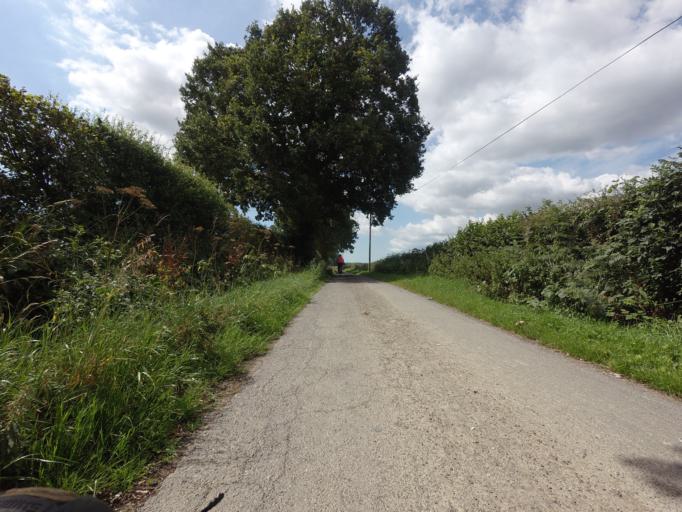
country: GB
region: England
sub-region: Kent
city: Stone
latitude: 51.0632
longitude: 0.7579
